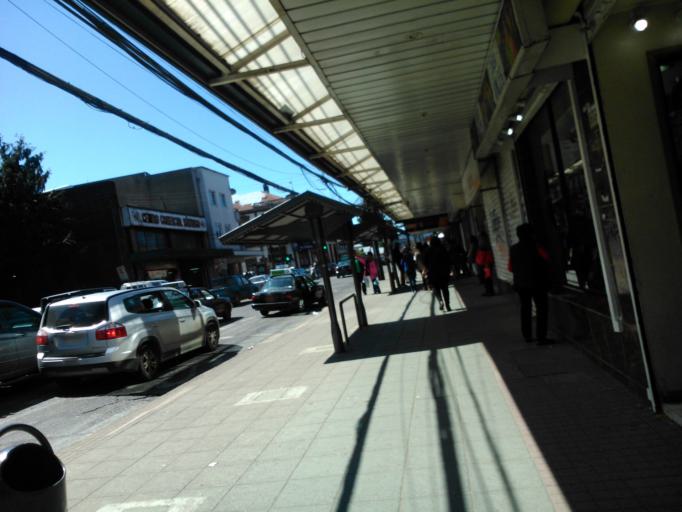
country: CL
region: Los Rios
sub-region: Provincia de Valdivia
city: Valdivia
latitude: -39.8154
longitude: -73.2451
